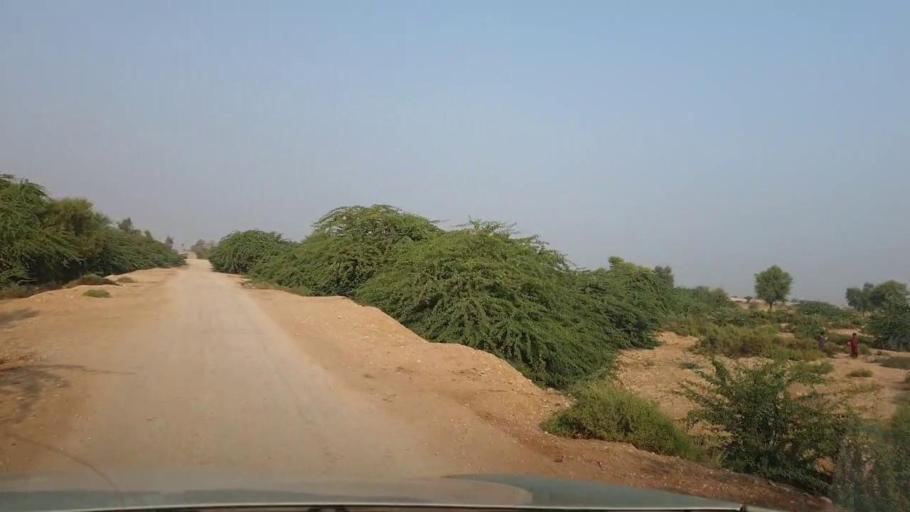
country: PK
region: Sindh
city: Sehwan
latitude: 26.3367
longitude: 67.7292
